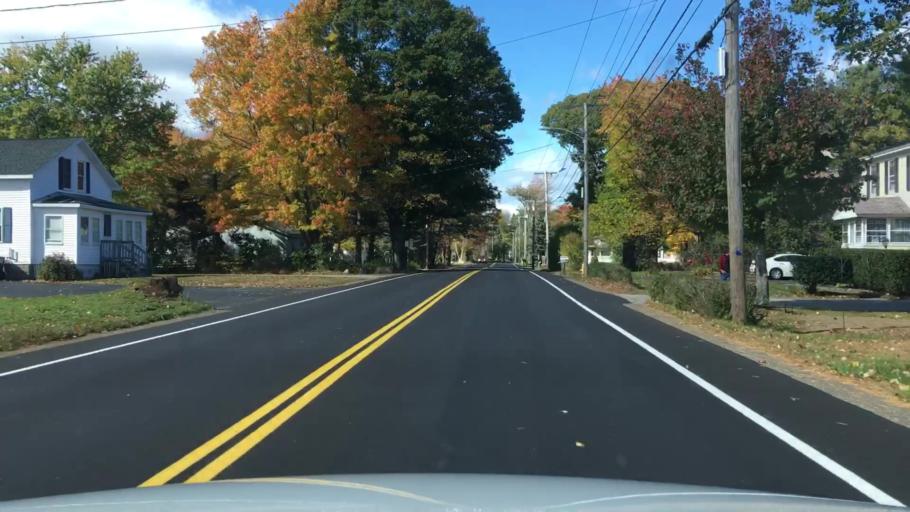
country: US
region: Maine
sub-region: York County
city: Biddeford
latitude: 43.4678
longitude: -70.4463
